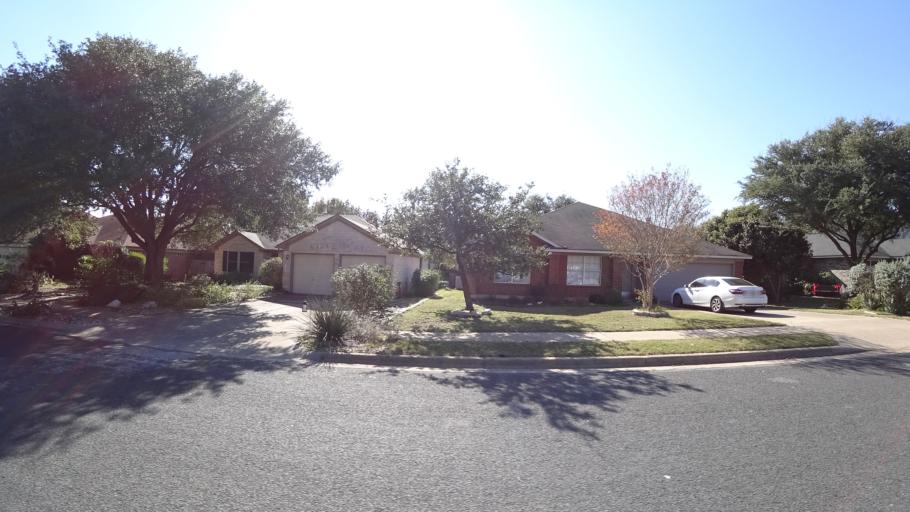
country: US
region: Texas
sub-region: Travis County
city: Shady Hollow
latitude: 30.2183
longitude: -97.8619
